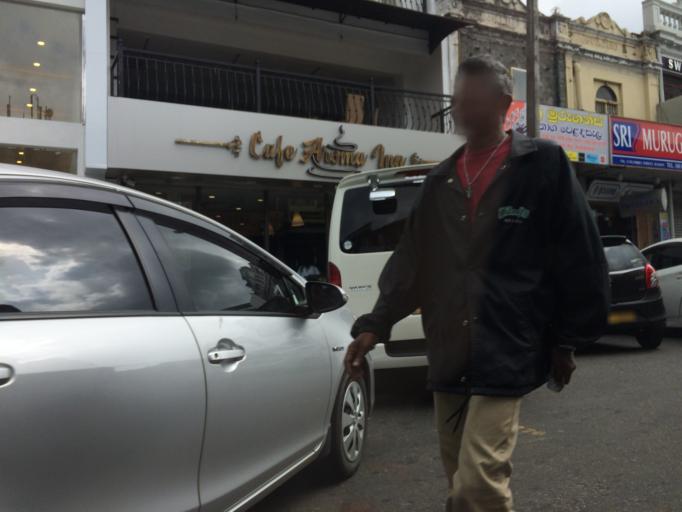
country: LK
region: Central
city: Kandy
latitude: 7.2943
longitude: 80.6372
